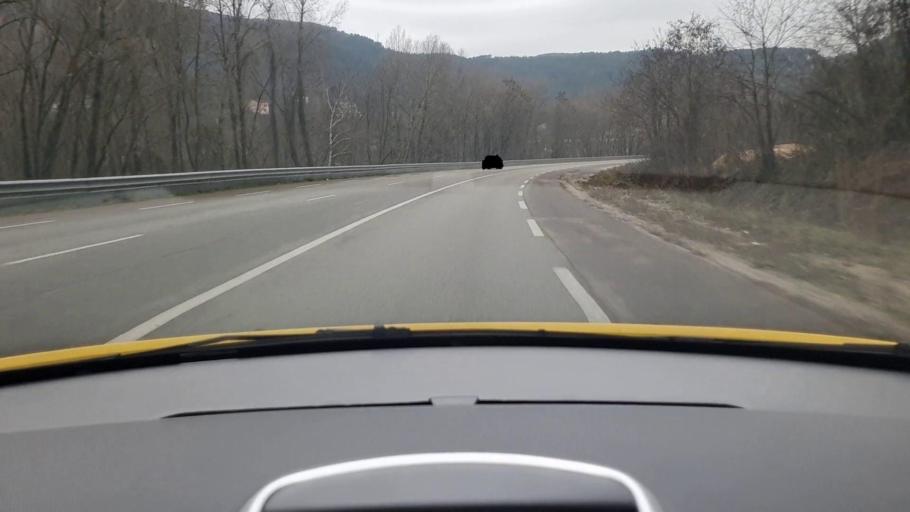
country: FR
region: Languedoc-Roussillon
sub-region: Departement du Gard
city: Molieres-sur-Ceze
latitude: 44.2637
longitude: 4.1637
